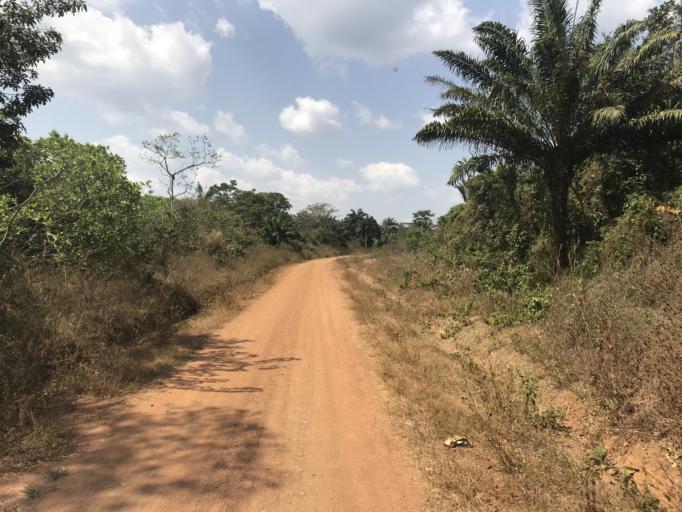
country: NG
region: Osun
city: Ifon
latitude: 7.9764
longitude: 4.5277
